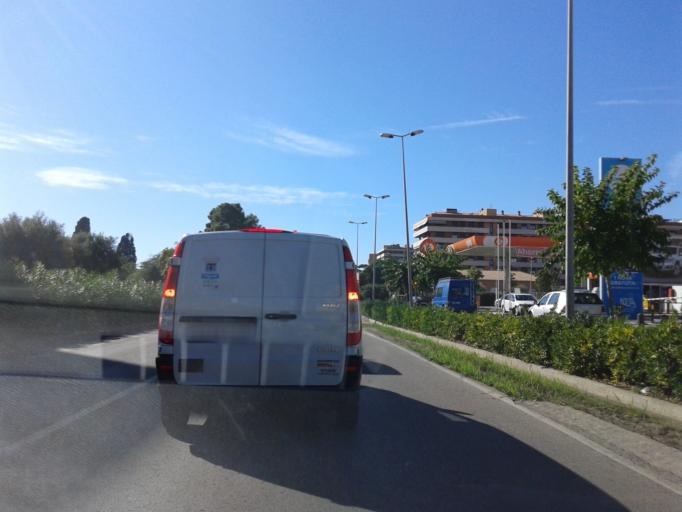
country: ES
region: Catalonia
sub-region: Provincia de Barcelona
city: Vilanova i la Geltru
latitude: 41.2191
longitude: 1.7172
